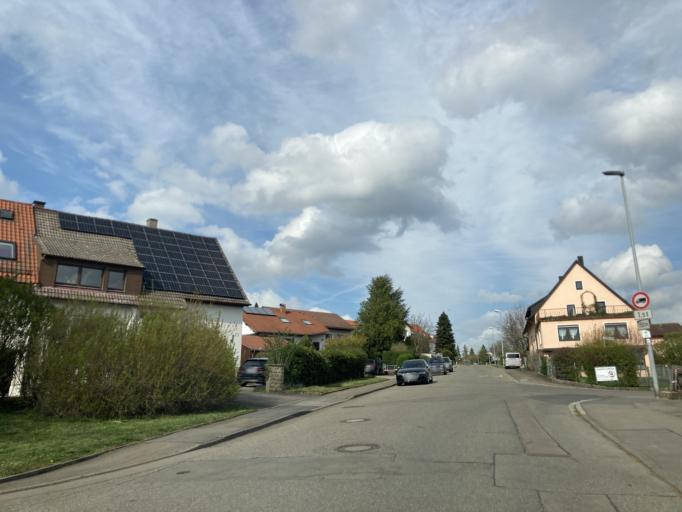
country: DE
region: Baden-Wuerttemberg
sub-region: Tuebingen Region
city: Dettenhausen
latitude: 48.6090
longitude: 9.1051
